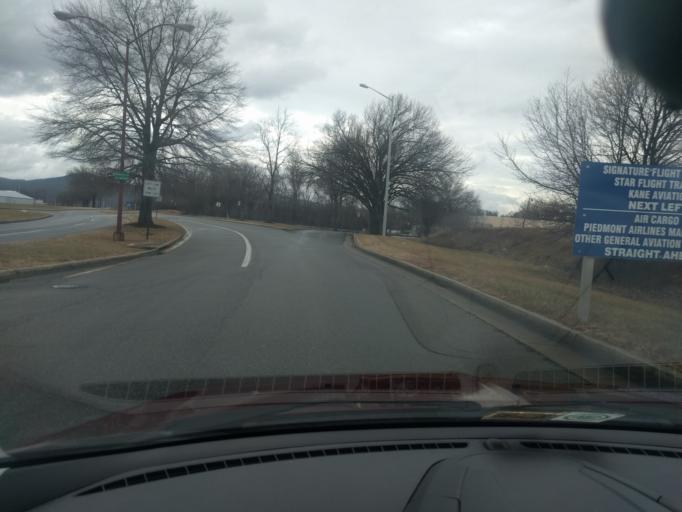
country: US
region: Virginia
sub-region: Roanoke County
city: Hollins
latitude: 37.3233
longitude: -79.9682
